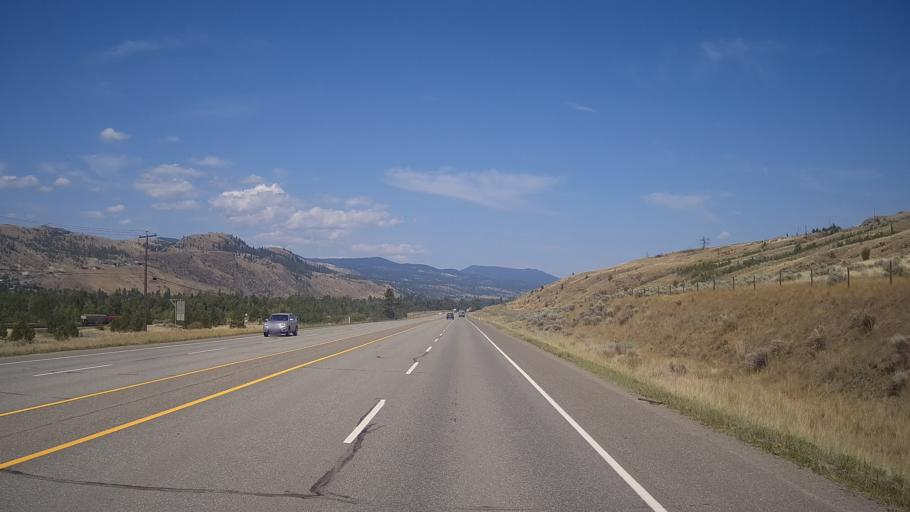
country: CA
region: British Columbia
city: Kamloops
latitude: 50.7599
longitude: -120.3307
